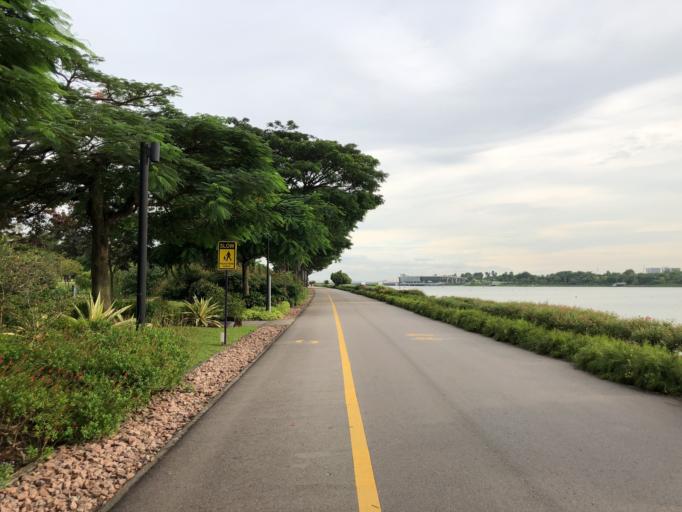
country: SG
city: Singapore
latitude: 1.2898
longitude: 103.8681
